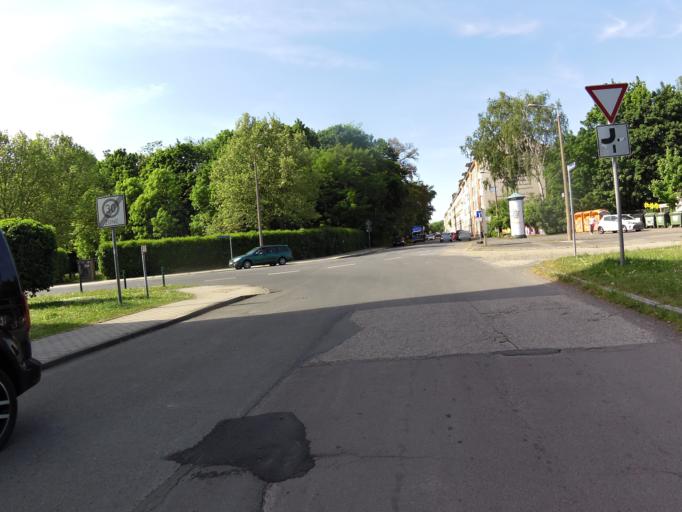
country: DE
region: Saxony
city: Leipzig
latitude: 51.3163
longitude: 12.4269
